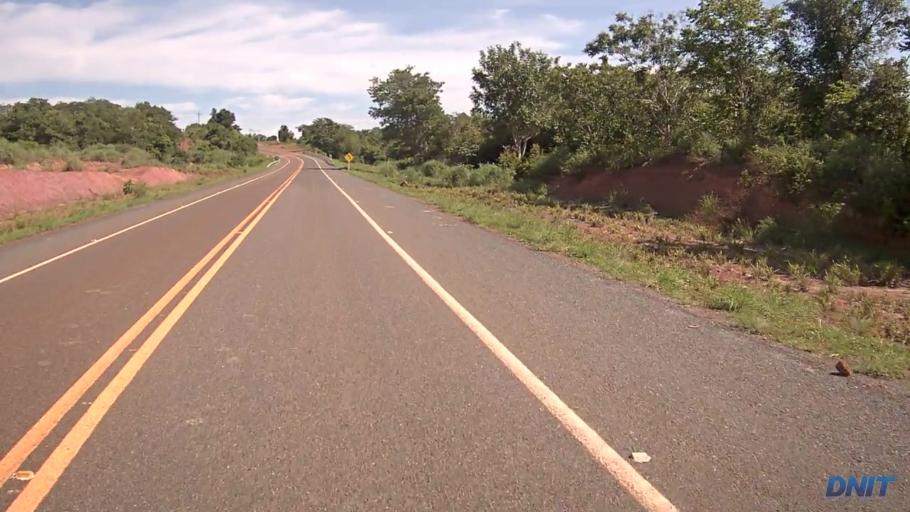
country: BR
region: Goias
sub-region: Sao Miguel Do Araguaia
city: Sao Miguel do Araguaia
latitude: -13.3264
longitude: -50.1563
